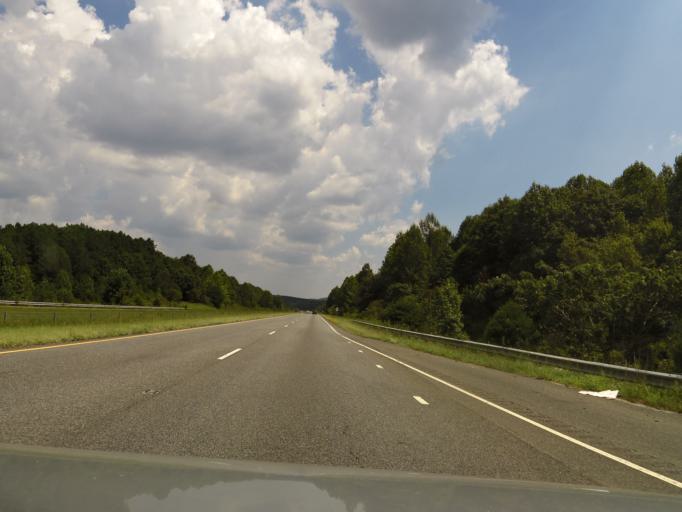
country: US
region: North Carolina
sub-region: Rutherford County
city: Rutherfordton
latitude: 35.2859
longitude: -82.0590
